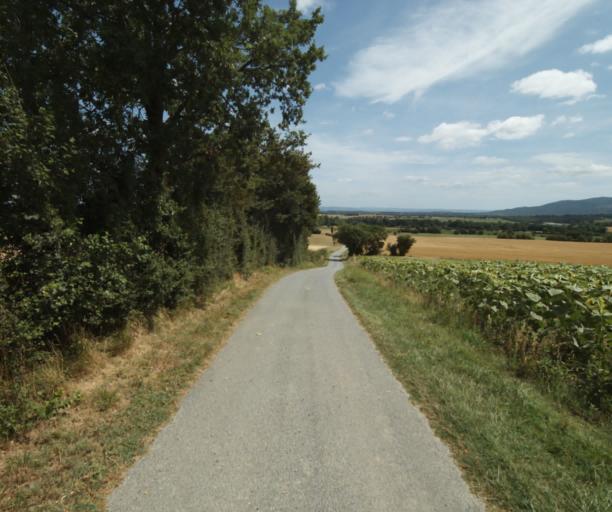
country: FR
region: Midi-Pyrenees
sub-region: Departement du Tarn
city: Soreze
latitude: 43.4882
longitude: 2.0719
